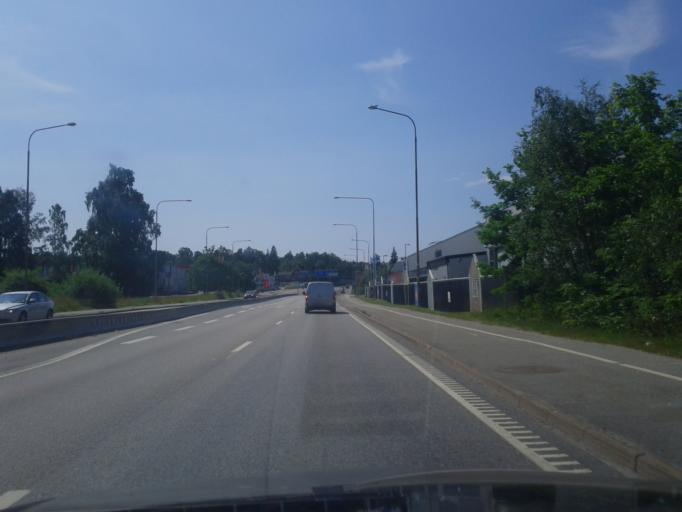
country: SE
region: Stockholm
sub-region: Huddinge Kommun
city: Huddinge
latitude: 59.2528
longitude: 18.0111
